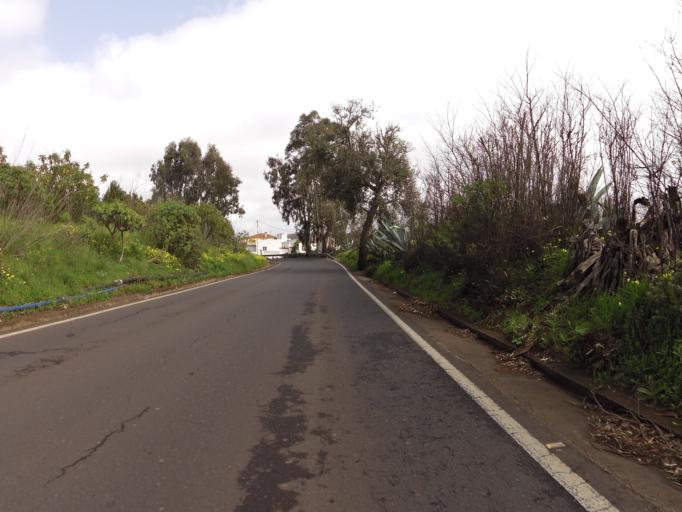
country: ES
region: Canary Islands
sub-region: Provincia de Las Palmas
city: Teror
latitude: 28.0741
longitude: -15.5393
